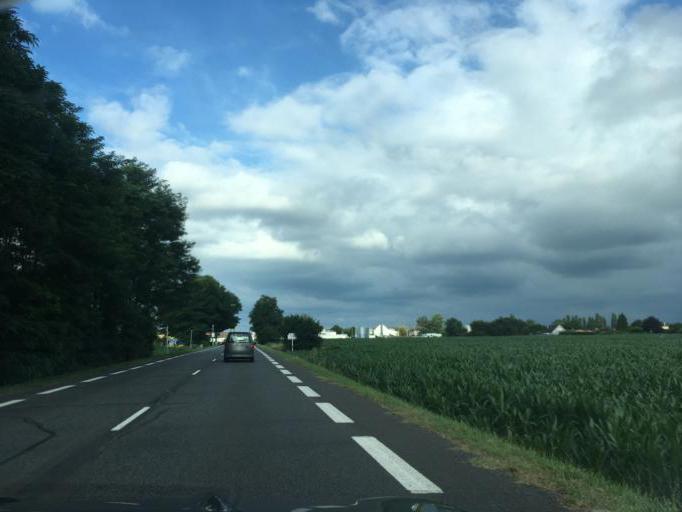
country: FR
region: Midi-Pyrenees
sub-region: Departement des Hautes-Pyrenees
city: Ibos
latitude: 43.2397
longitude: 0.0246
